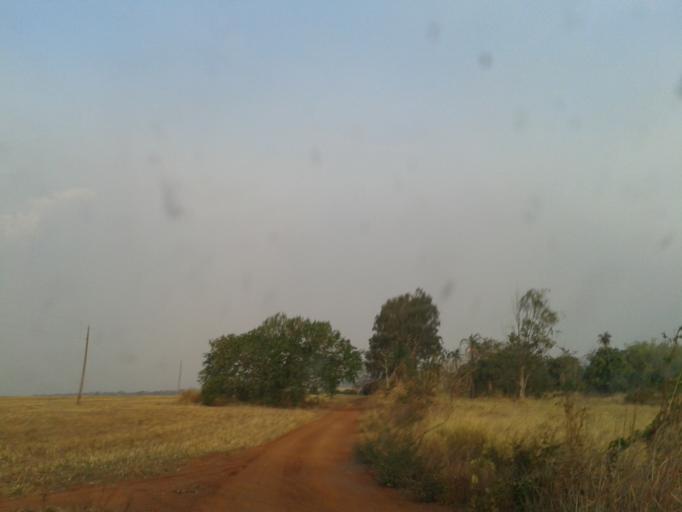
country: BR
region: Minas Gerais
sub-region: Capinopolis
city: Capinopolis
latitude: -18.8083
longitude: -49.7301
